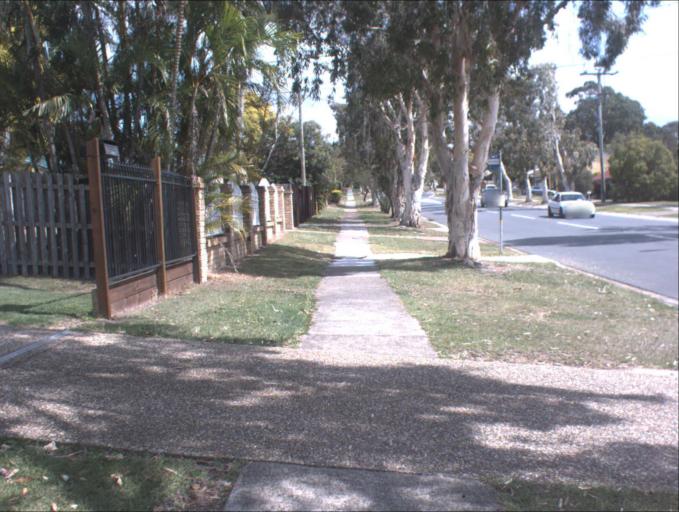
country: AU
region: Queensland
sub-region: Brisbane
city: Sunnybank Hills
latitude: -27.6679
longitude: 153.0427
